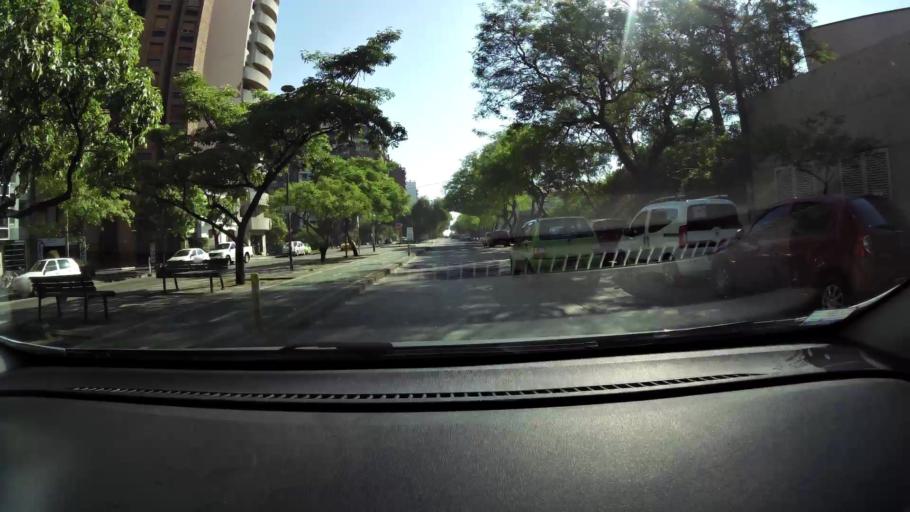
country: AR
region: Cordoba
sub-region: Departamento de Capital
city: Cordoba
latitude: -31.4279
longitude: -64.1834
